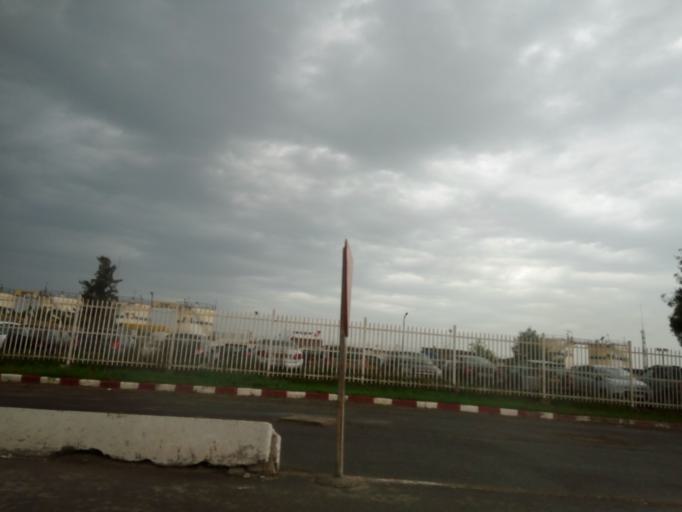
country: DZ
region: Alger
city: Dar el Beida
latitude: 36.7026
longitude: 3.2100
